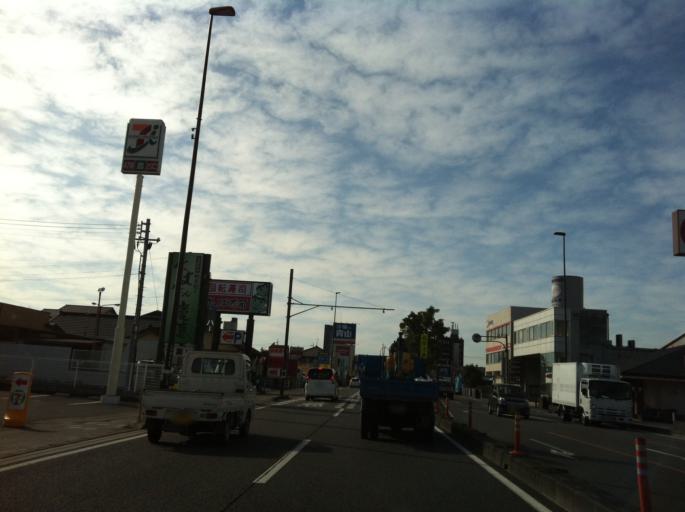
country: JP
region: Shizuoka
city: Shizuoka-shi
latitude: 35.0121
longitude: 138.4516
